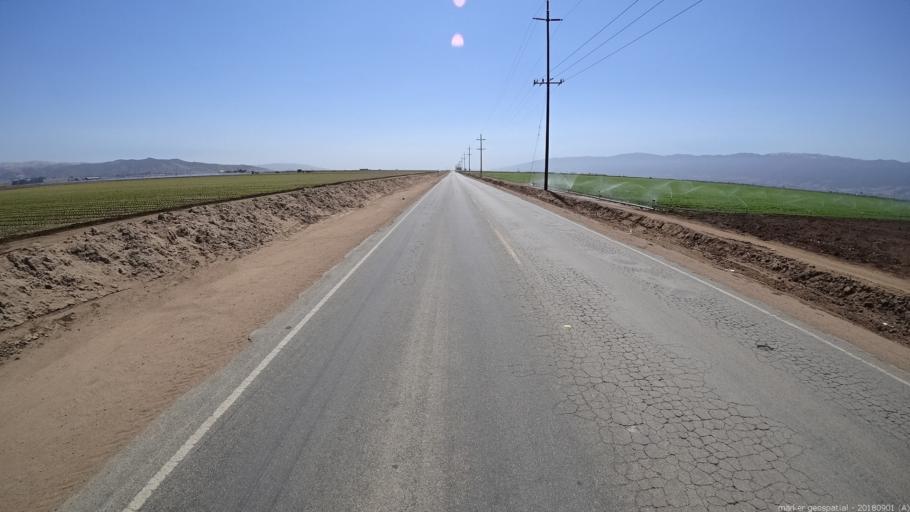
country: US
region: California
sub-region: Monterey County
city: Chualar
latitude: 36.5993
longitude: -121.5094
